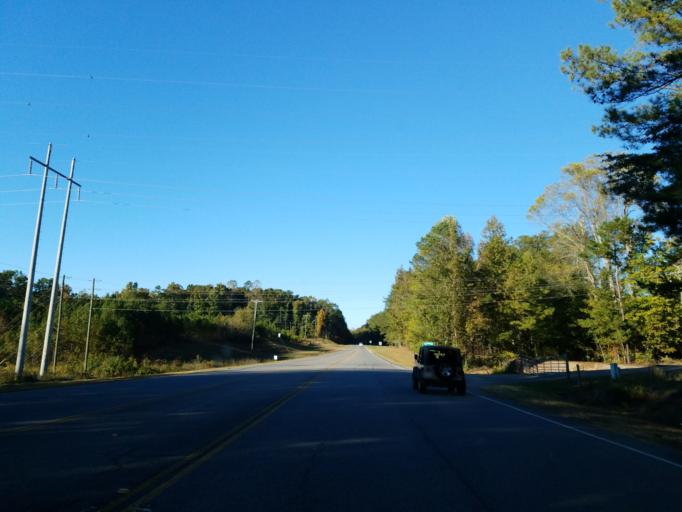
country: US
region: Georgia
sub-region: Pickens County
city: Nelson
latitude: 34.3706
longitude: -84.3723
